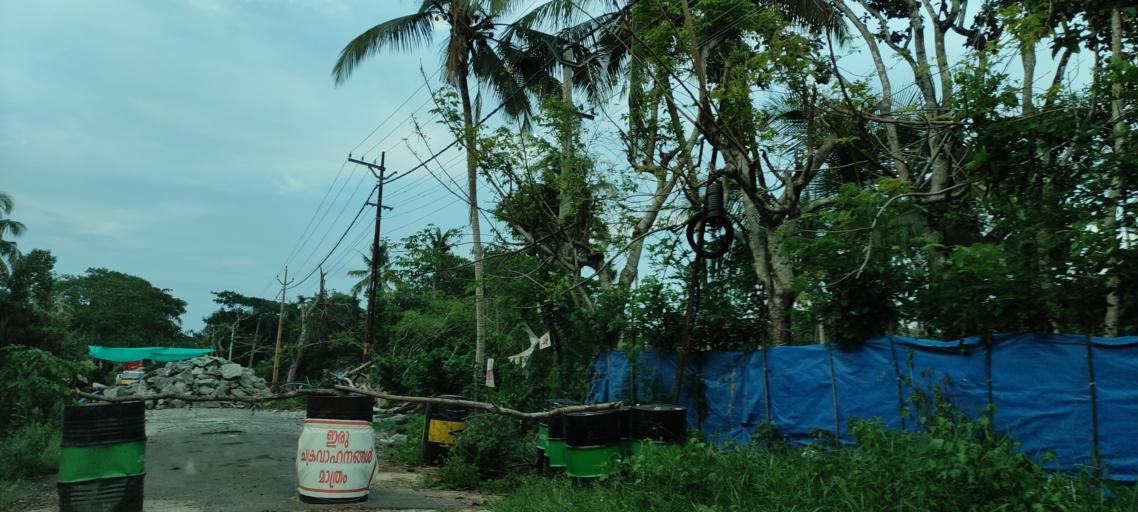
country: IN
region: Kerala
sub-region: Alappuzha
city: Shertallai
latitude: 9.6929
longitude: 76.3554
